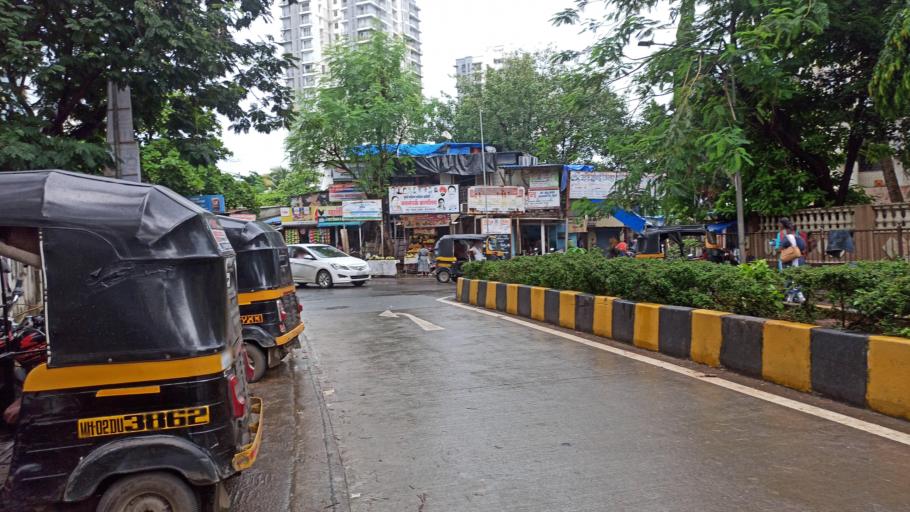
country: IN
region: Maharashtra
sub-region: Mumbai Suburban
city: Borivli
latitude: 19.2607
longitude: 72.8528
